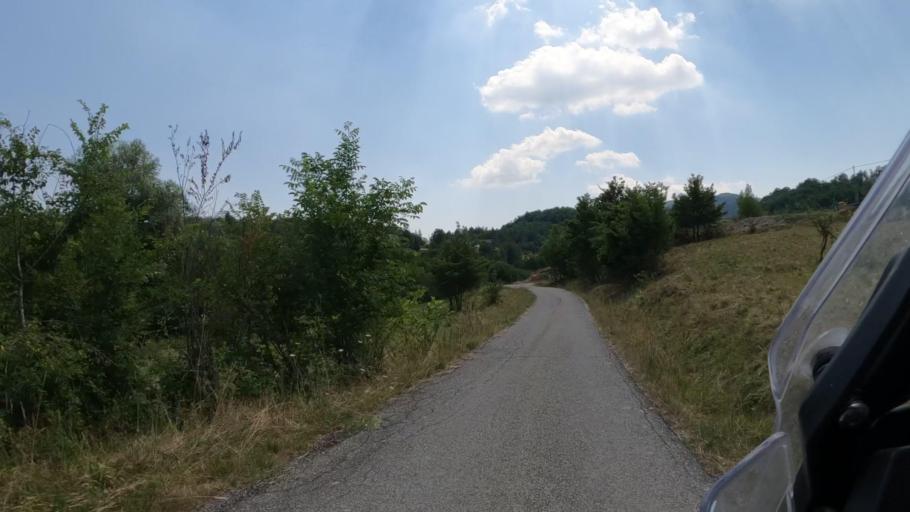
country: IT
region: Piedmont
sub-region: Provincia di Alessandria
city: Cassinelle-Concentrico
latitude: 44.5729
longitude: 8.5561
